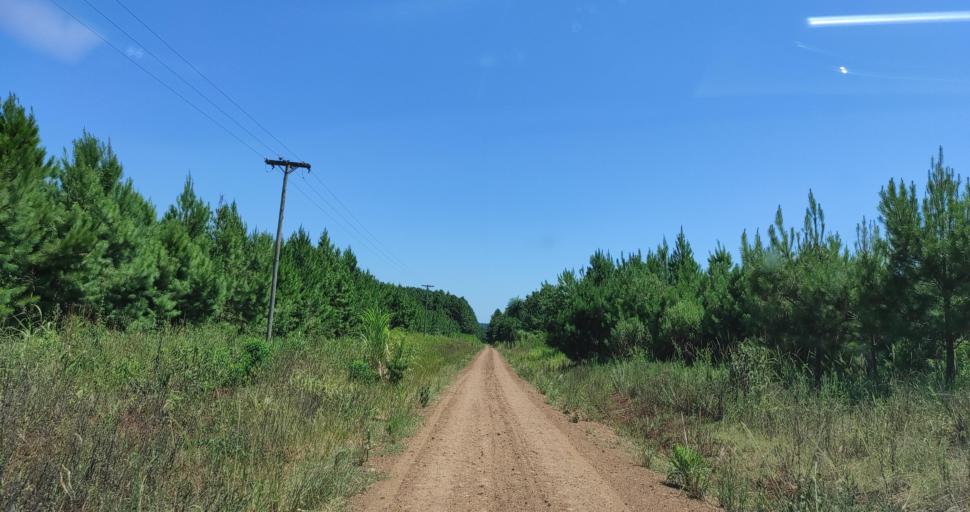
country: AR
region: Misiones
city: Capiovi
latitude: -26.9307
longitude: -55.0968
